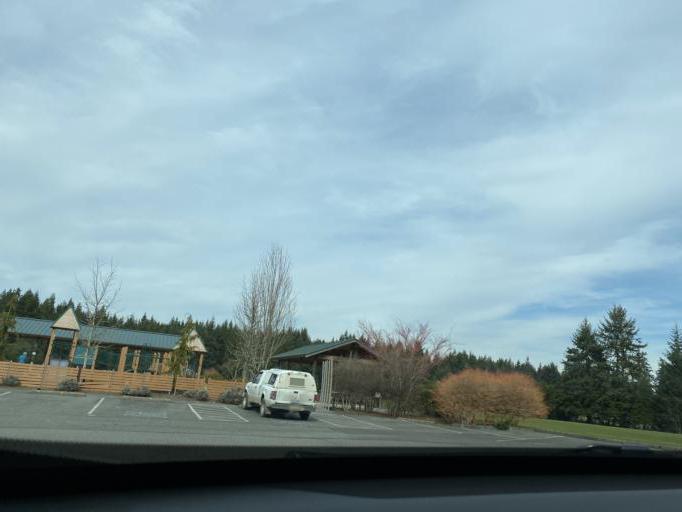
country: US
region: Washington
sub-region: Island County
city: Langley
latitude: 48.0068
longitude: -122.3983
